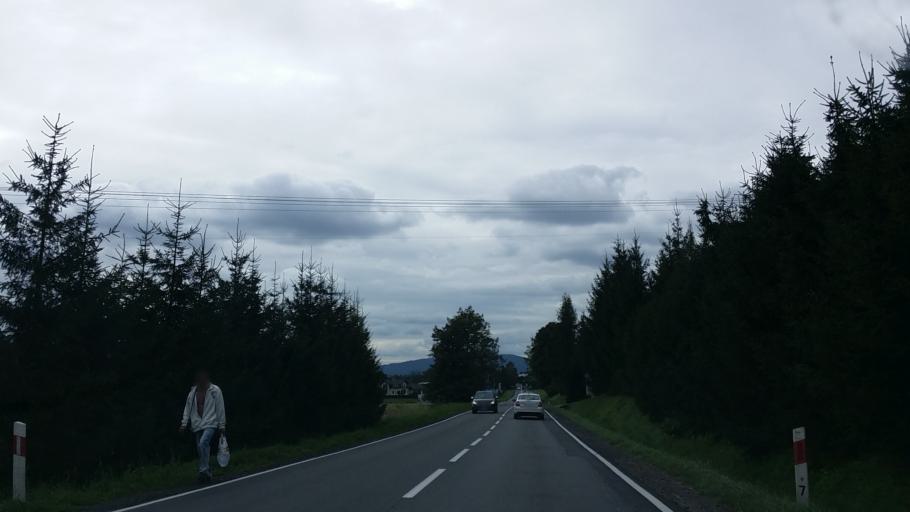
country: PL
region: Lesser Poland Voivodeship
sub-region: Powiat wadowicki
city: Radocza
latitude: 49.9215
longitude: 19.4791
